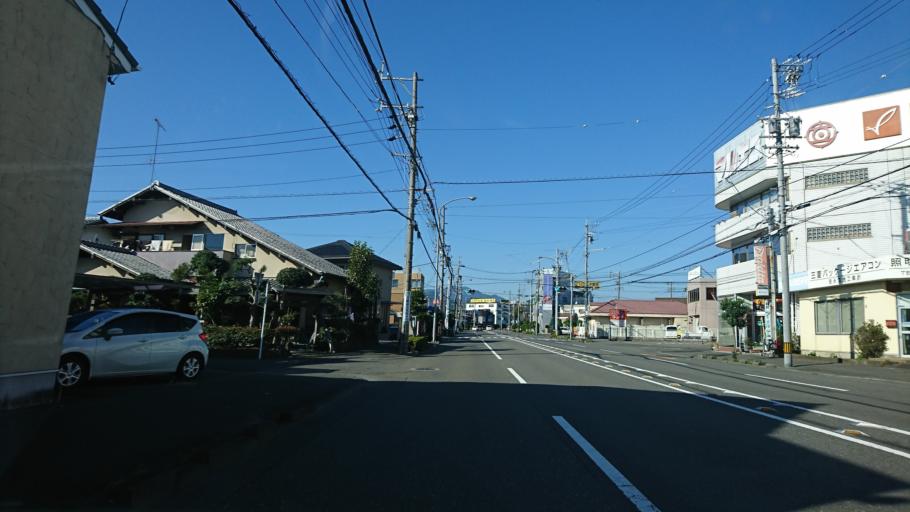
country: JP
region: Shizuoka
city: Shizuoka-shi
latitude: 34.9887
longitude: 138.3653
